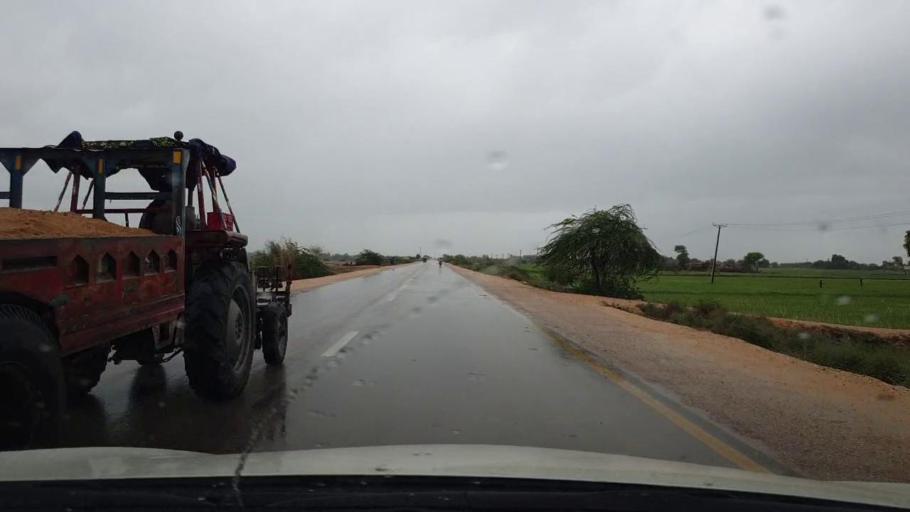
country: PK
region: Sindh
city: Kario
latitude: 24.6534
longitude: 68.5652
